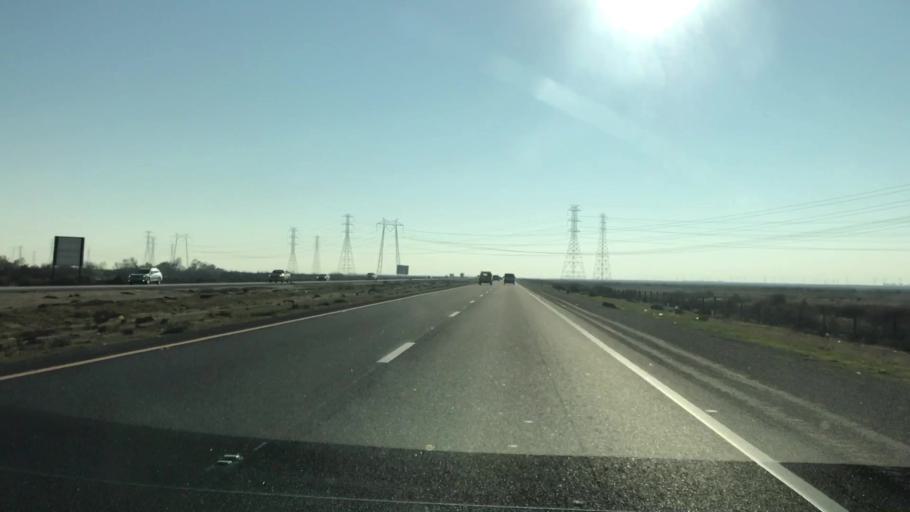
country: US
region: California
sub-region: Kern County
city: Buttonwillow
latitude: 35.3907
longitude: -119.3864
